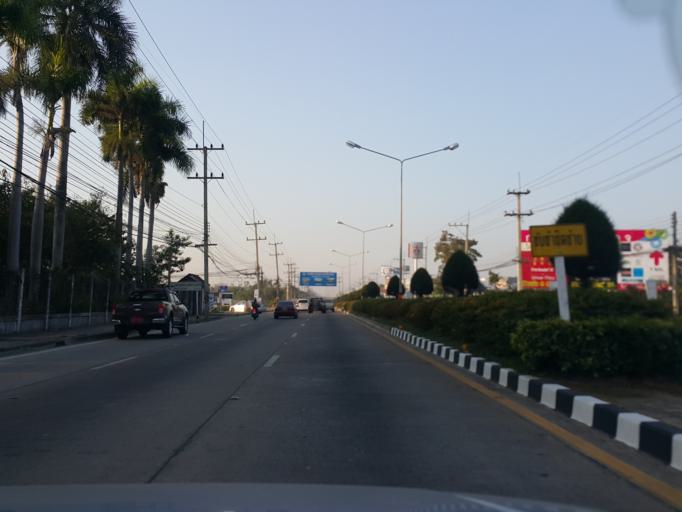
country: TH
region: Chiang Mai
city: Hang Dong
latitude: 18.7119
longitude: 98.9382
